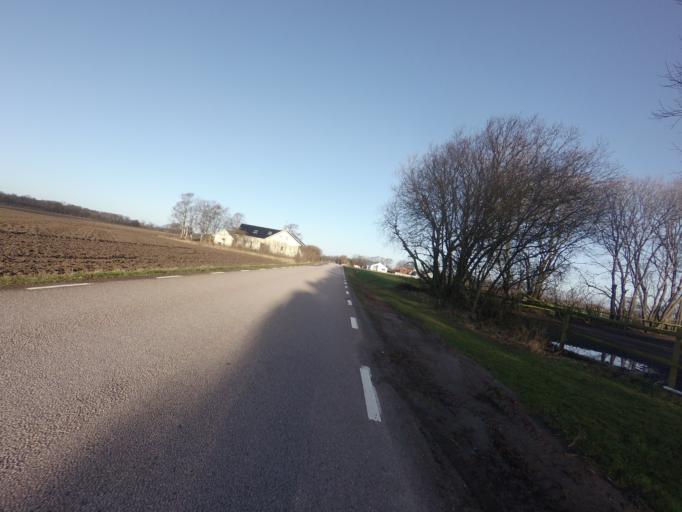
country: SE
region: Skane
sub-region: Helsingborg
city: Odakra
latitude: 56.1140
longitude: 12.6822
